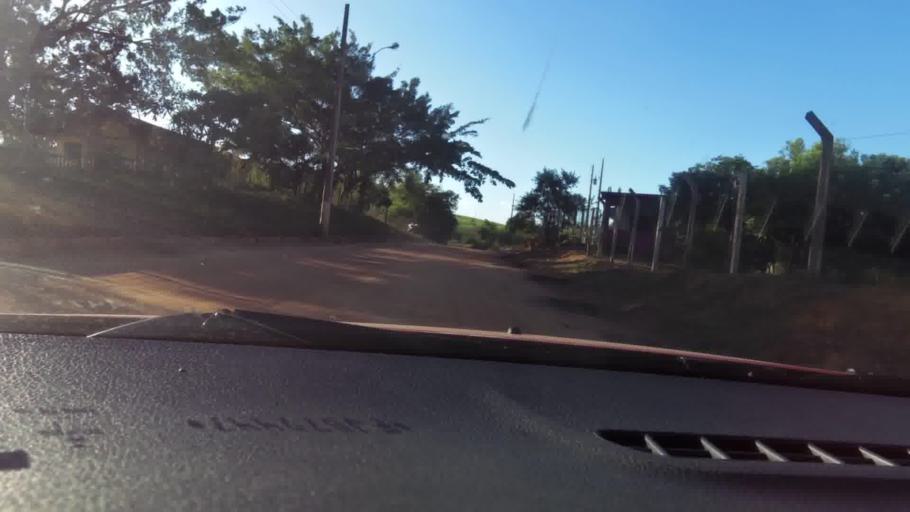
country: BR
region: Espirito Santo
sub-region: Guarapari
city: Guarapari
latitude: -20.5502
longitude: -40.4221
